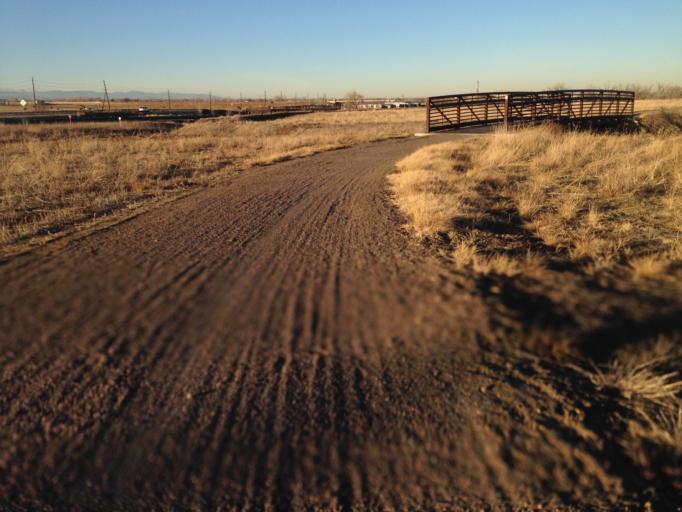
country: US
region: Colorado
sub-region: Broomfield County
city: Broomfield
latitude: 39.9502
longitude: -105.0891
